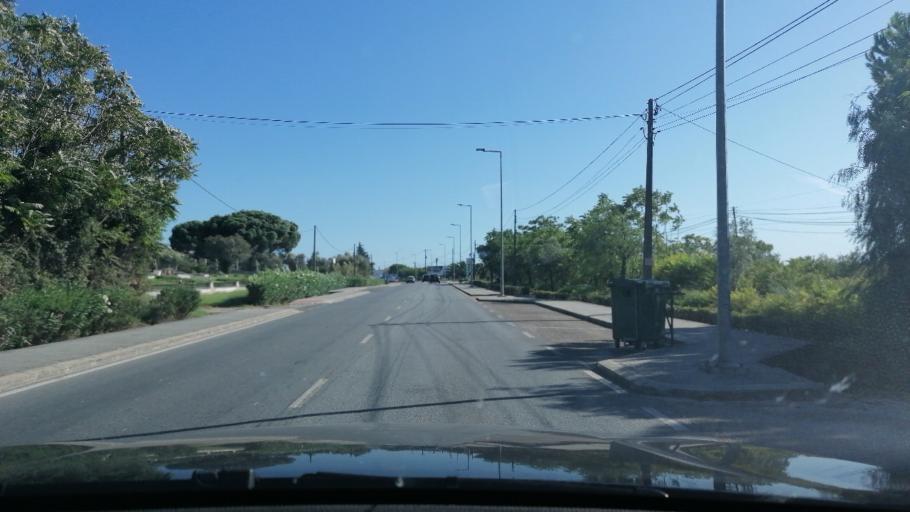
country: PT
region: Setubal
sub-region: Alcacer do Sal
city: Alcacer do Sal
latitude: 38.3827
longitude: -8.5134
